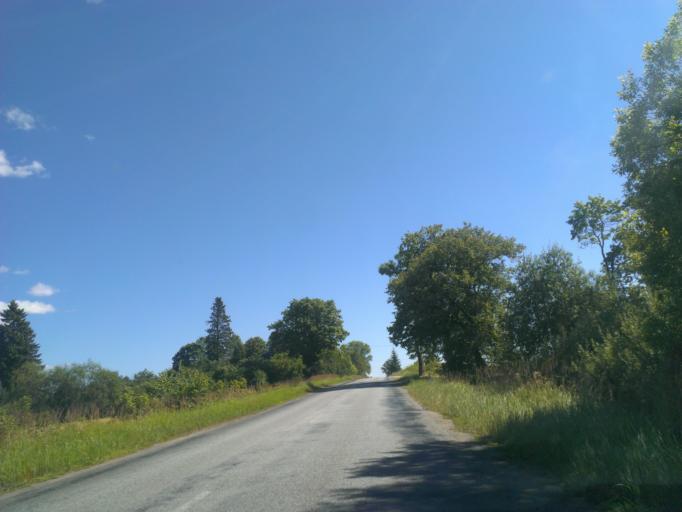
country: LV
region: Malpils
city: Malpils
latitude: 57.0220
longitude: 24.8439
